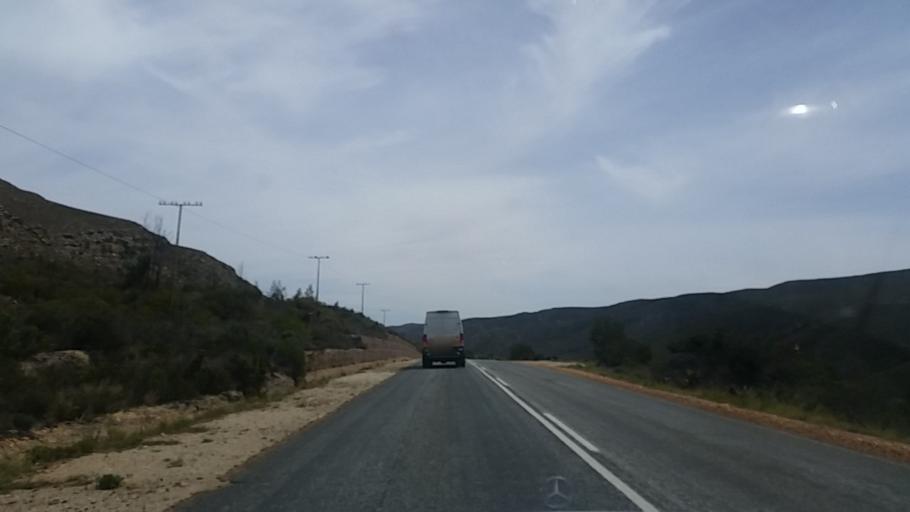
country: ZA
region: Western Cape
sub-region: Eden District Municipality
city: Knysna
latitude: -33.7427
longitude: 23.0168
